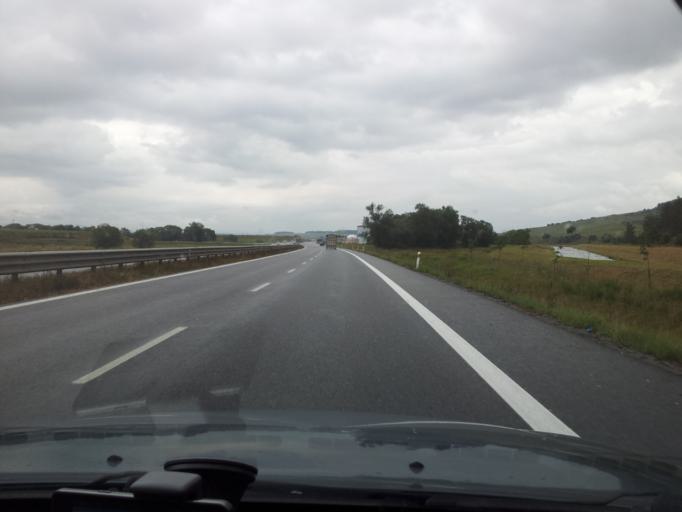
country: SK
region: Presovsky
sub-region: Okres Poprad
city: Poprad
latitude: 49.0906
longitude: 20.3377
